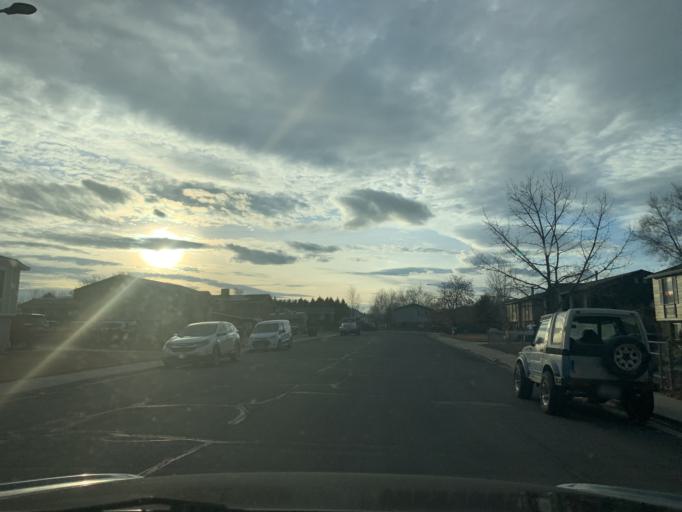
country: US
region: Utah
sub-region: Utah County
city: Provo
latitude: 40.2181
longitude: -111.6709
